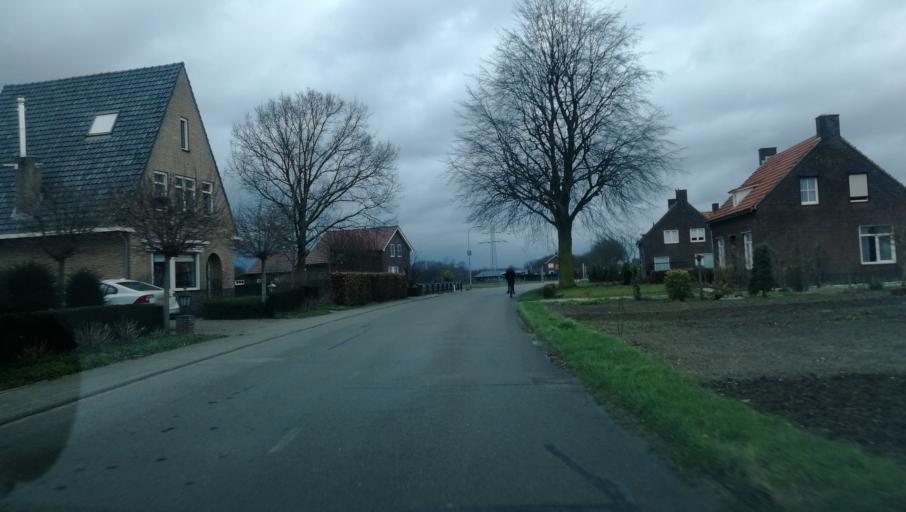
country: NL
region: Limburg
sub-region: Gemeente Beesel
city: Reuver
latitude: 51.2967
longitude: 6.0582
